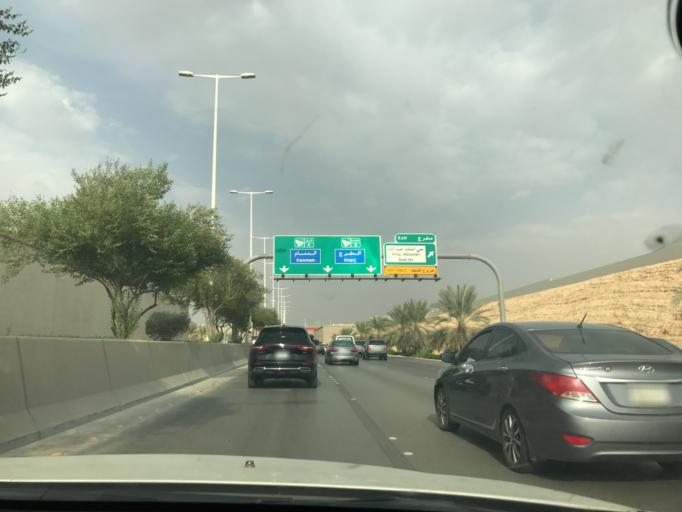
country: SA
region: Ar Riyad
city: Riyadh
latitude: 24.7328
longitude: 46.7334
